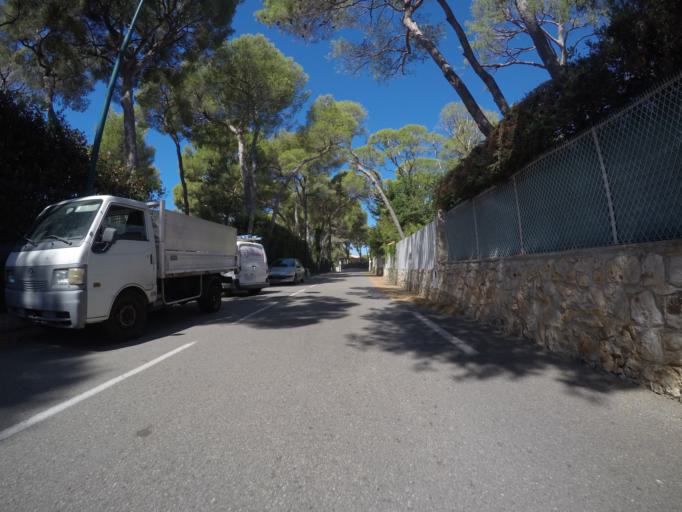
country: FR
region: Provence-Alpes-Cote d'Azur
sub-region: Departement des Alpes-Maritimes
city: Saint-Jean-Cap-Ferrat
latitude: 43.6776
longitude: 7.3296
